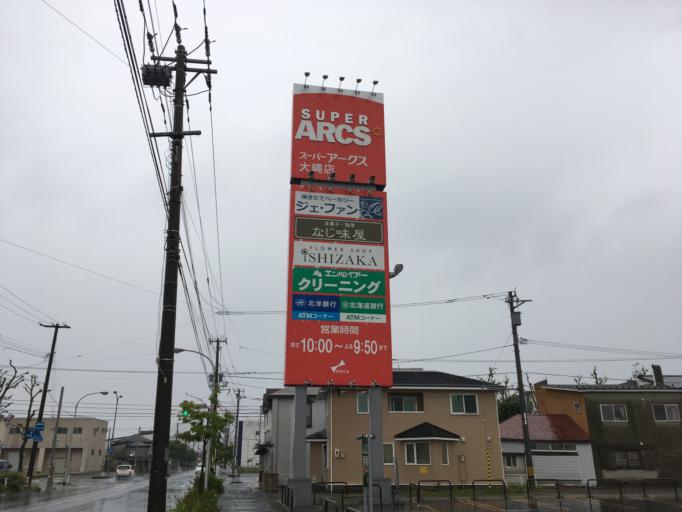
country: JP
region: Hokkaido
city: Hakodate
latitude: 41.7801
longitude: 140.7362
